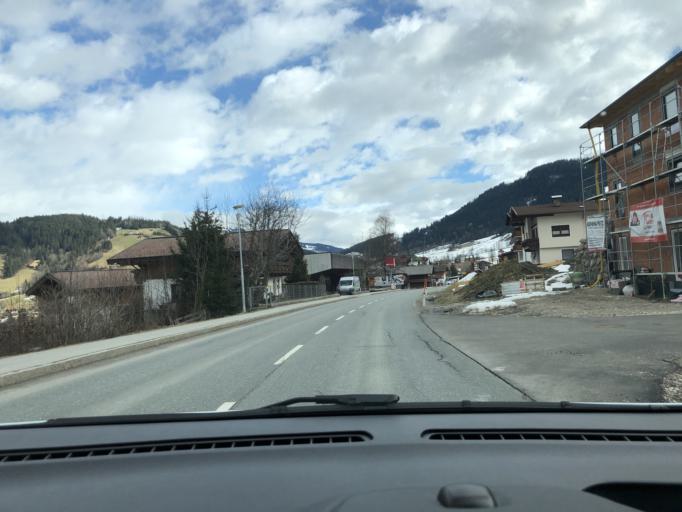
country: AT
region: Tyrol
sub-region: Politischer Bezirk Kufstein
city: Worgl
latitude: 47.4493
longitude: 12.0815
